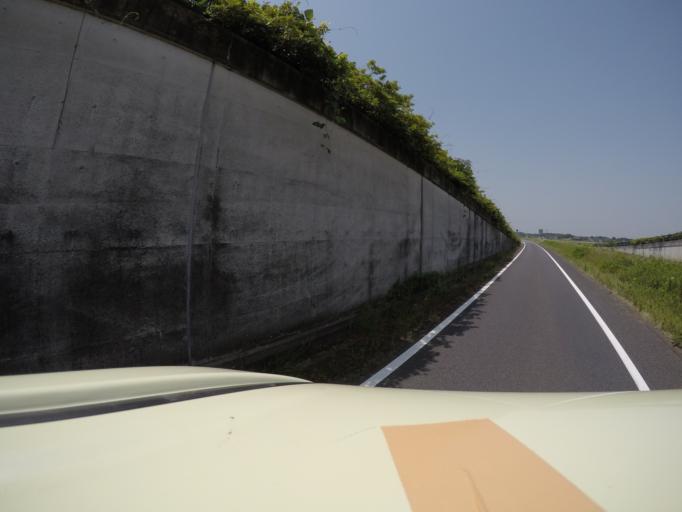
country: JP
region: Ibaraki
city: Mitsukaido
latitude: 36.0392
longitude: 139.9697
